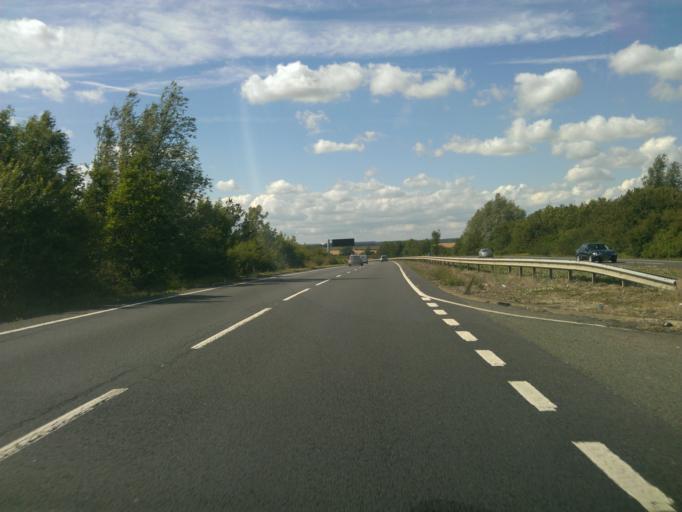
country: GB
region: England
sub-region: Northamptonshire
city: Thrapston
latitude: 52.3819
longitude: -0.4857
